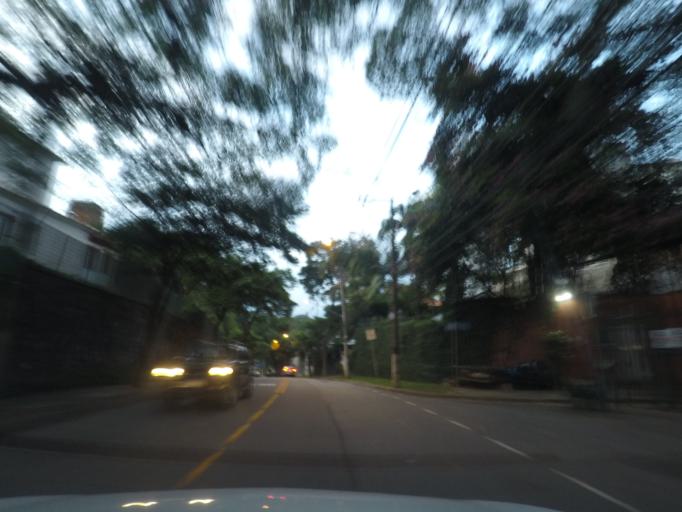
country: BR
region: Sao Paulo
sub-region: Taboao Da Serra
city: Taboao da Serra
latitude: -23.6073
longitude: -46.7095
